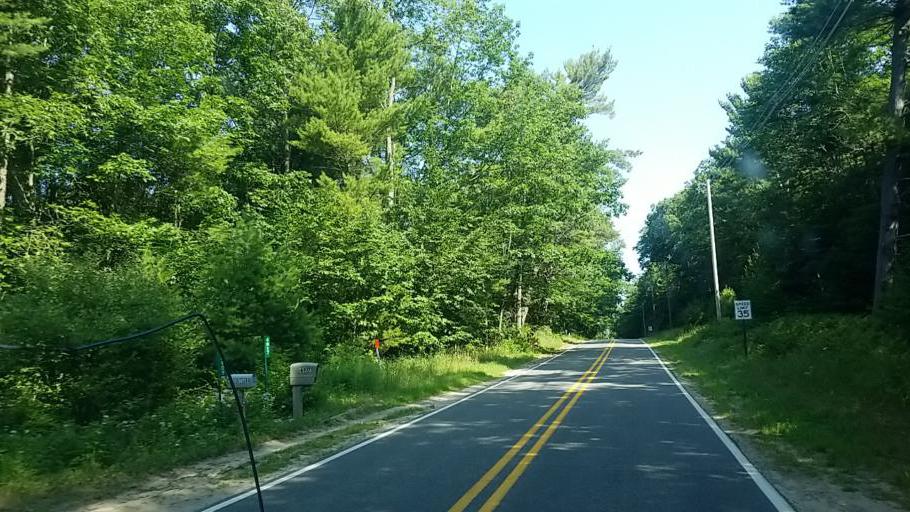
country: US
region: Michigan
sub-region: Muskegon County
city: Montague
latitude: 43.3479
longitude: -86.4077
